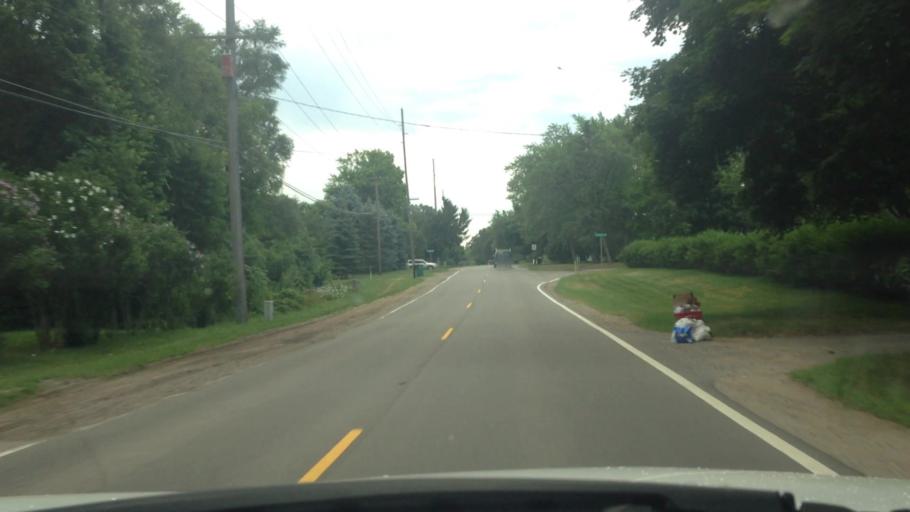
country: US
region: Michigan
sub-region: Oakland County
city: Waterford
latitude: 42.7038
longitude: -83.3488
